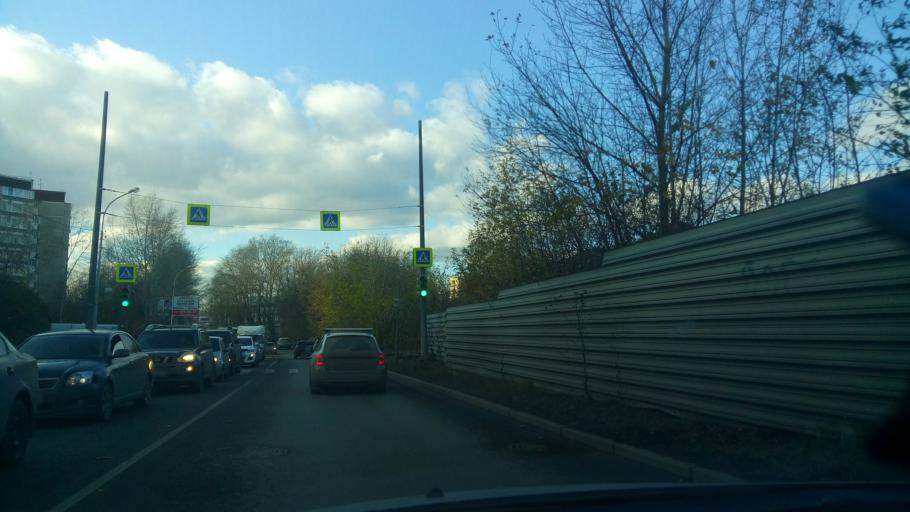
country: RU
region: Sverdlovsk
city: Yekaterinburg
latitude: 56.8568
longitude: 60.5722
